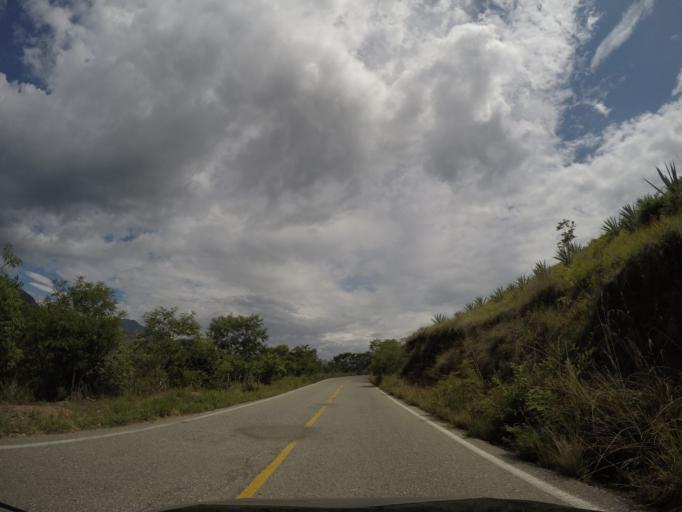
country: MX
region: Oaxaca
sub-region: San Jeronimo Coatlan
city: San Cristobal Honduras
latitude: 16.4309
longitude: -97.0678
